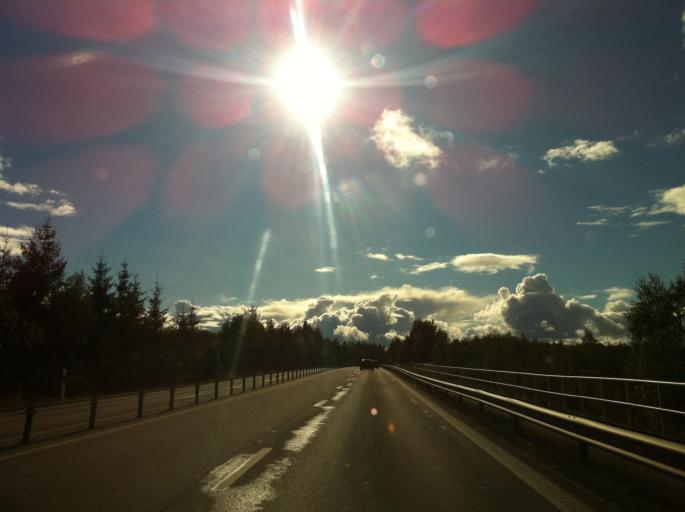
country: SE
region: Skane
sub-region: Hassleholms Kommun
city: Sosdala
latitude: 56.1610
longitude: 13.5715
